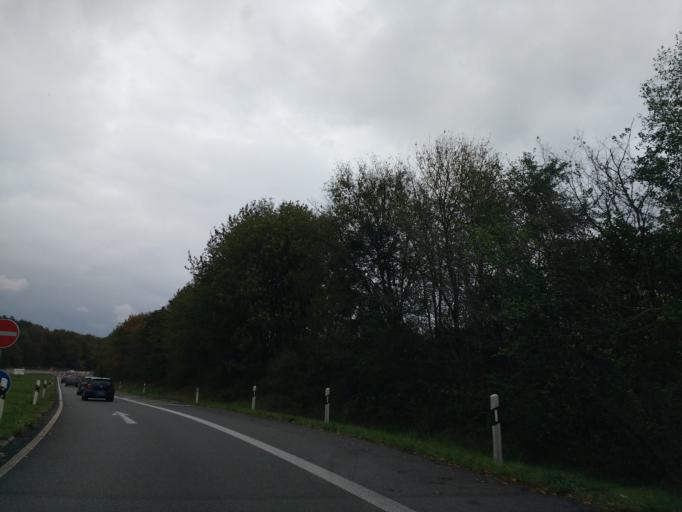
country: DE
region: North Rhine-Westphalia
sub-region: Regierungsbezirk Dusseldorf
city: Alpen
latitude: 51.5634
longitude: 6.4909
